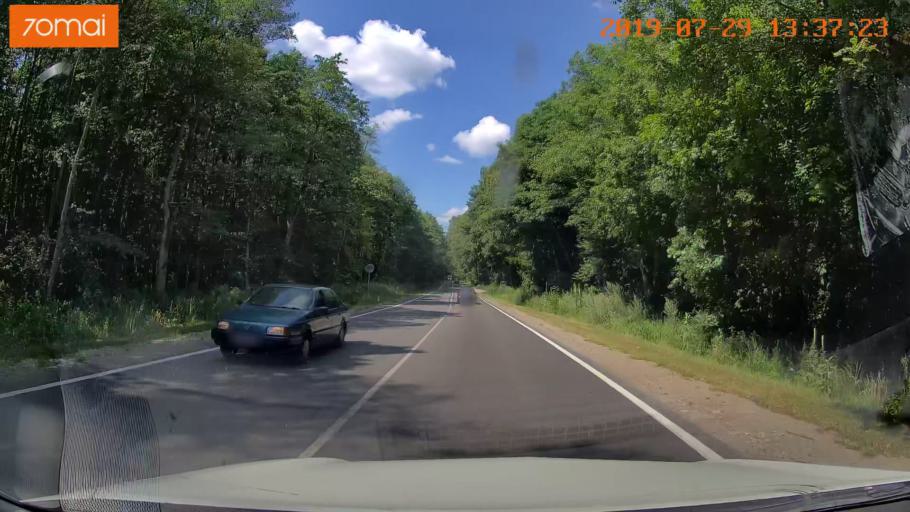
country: RU
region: Kaliningrad
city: Volochayevskoye
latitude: 54.7141
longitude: 20.1850
